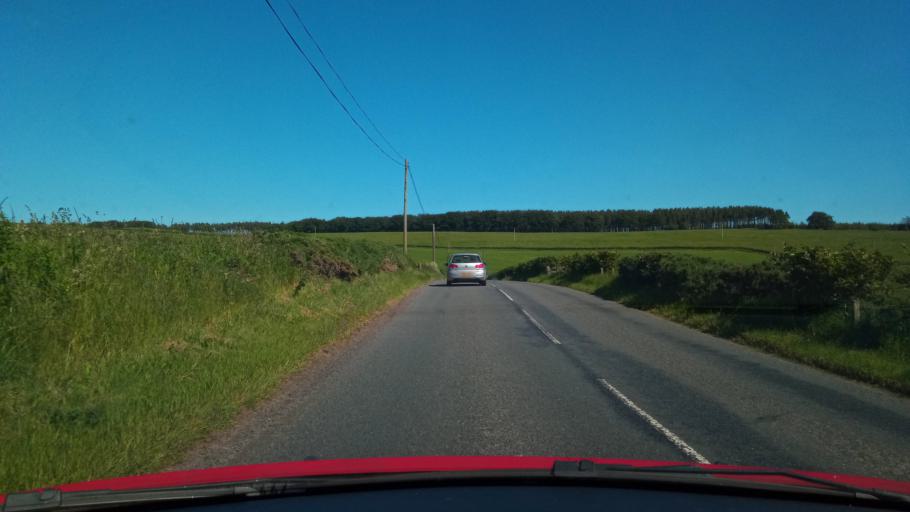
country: GB
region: Scotland
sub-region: The Scottish Borders
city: Duns
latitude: 55.8325
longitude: -2.3305
